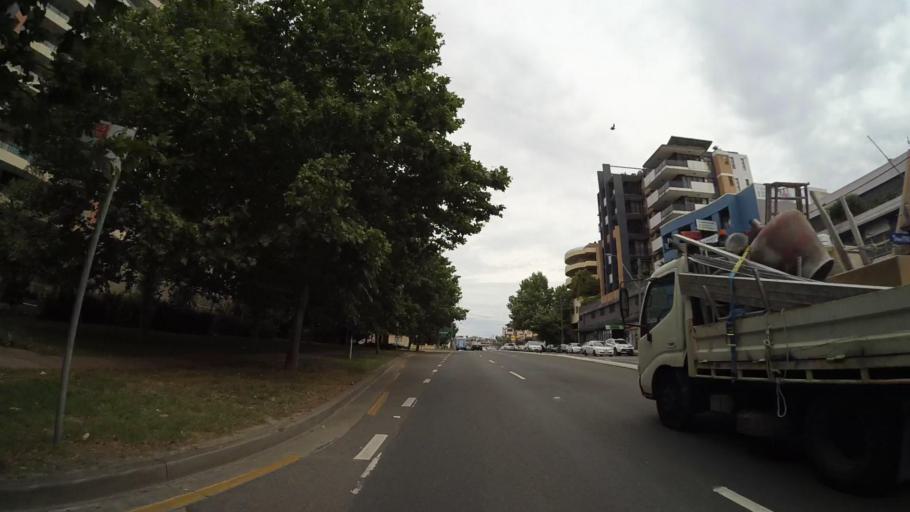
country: AU
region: New South Wales
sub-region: Rockdale
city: Banksia
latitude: -33.9579
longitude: 151.1379
